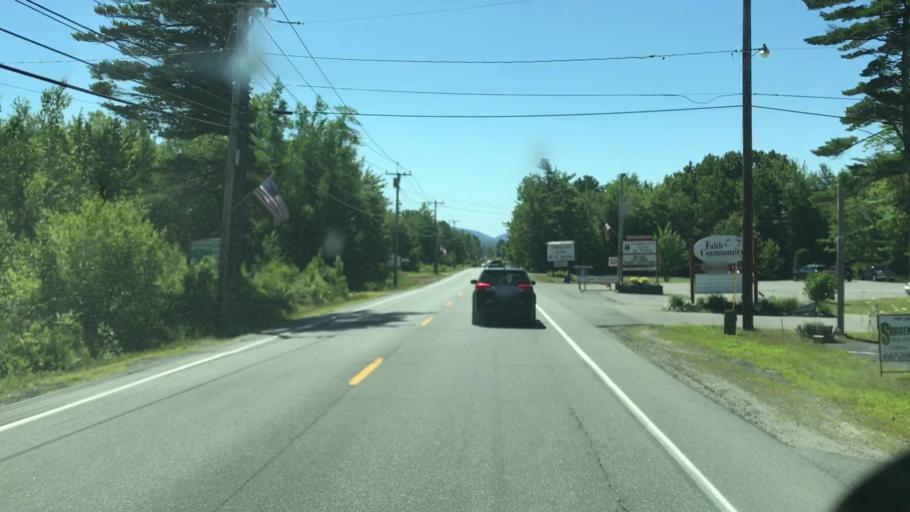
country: US
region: Maine
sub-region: Hancock County
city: Ellsworth
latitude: 44.5079
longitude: -68.3892
